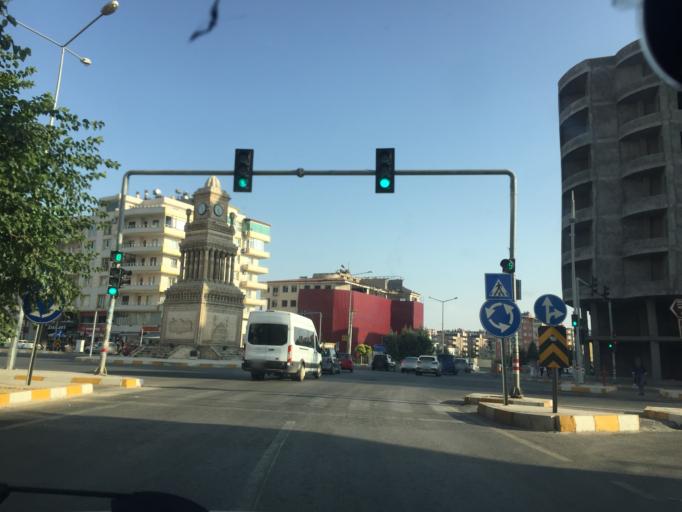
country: TR
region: Mardin
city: Midyat
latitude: 37.4229
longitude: 41.3463
